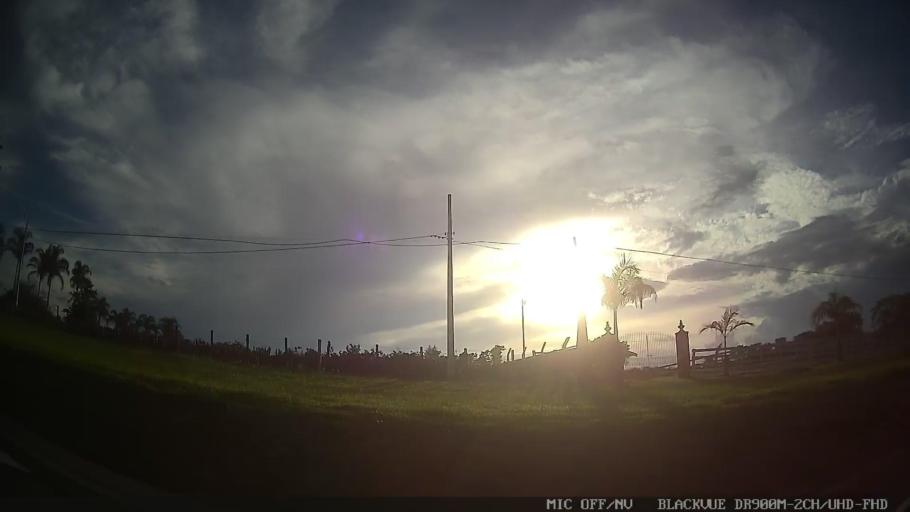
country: BR
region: Sao Paulo
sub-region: Tiete
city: Tiete
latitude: -23.1625
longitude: -47.6478
